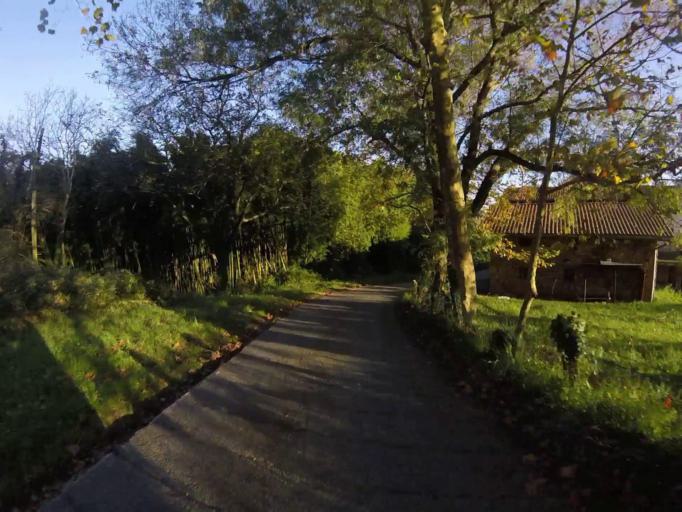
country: ES
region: Basque Country
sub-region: Provincia de Guipuzcoa
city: Lasarte
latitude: 43.2844
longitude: -2.0107
